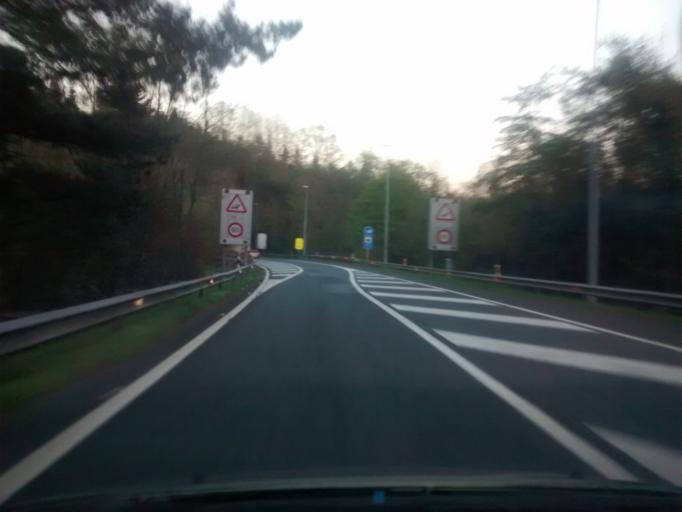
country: ES
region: Basque Country
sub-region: Provincia de Guipuzcoa
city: San Sebastian
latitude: 43.2986
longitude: -1.9812
